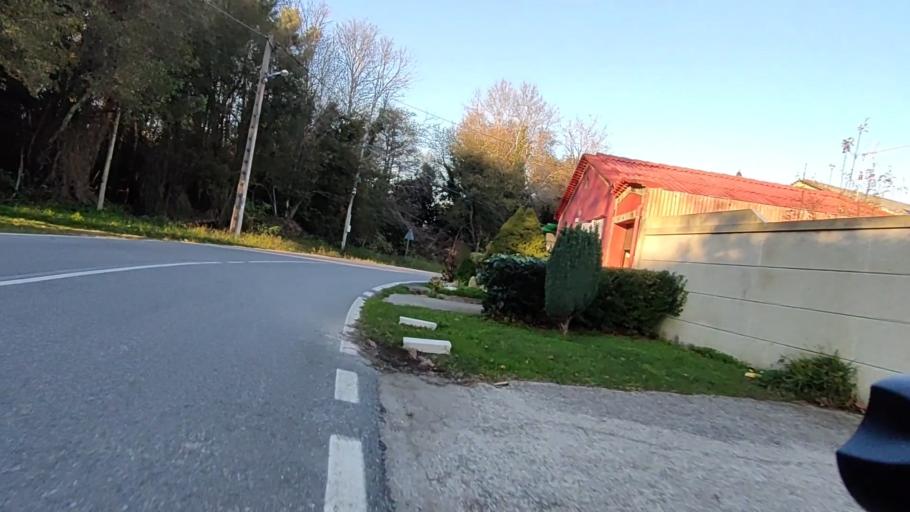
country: ES
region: Galicia
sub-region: Provincia da Coruna
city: Rianxo
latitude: 42.6370
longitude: -8.8559
